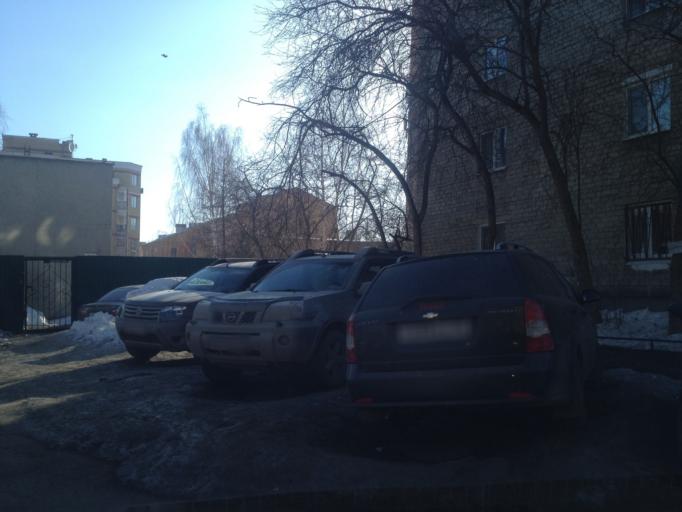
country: RU
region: Sverdlovsk
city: Yekaterinburg
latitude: 56.8120
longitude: 60.6042
